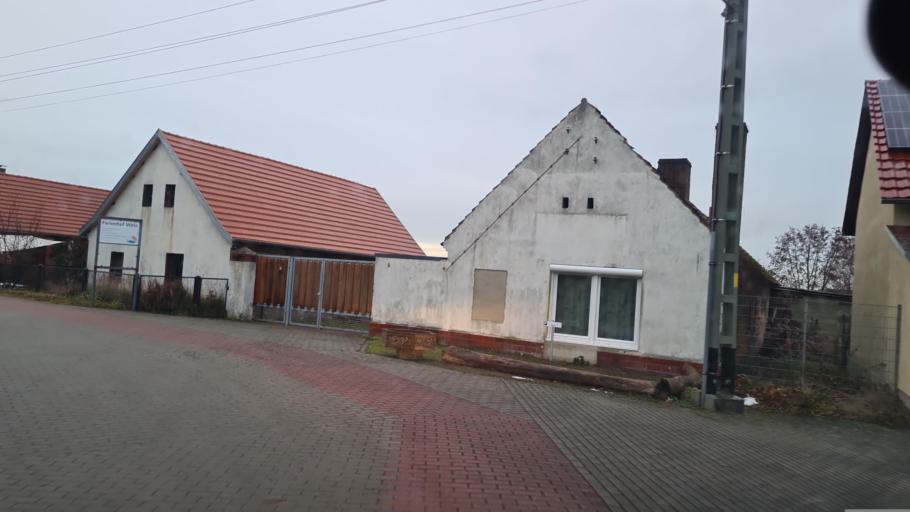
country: DE
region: Brandenburg
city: Neupetershain
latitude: 51.6260
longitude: 14.1656
